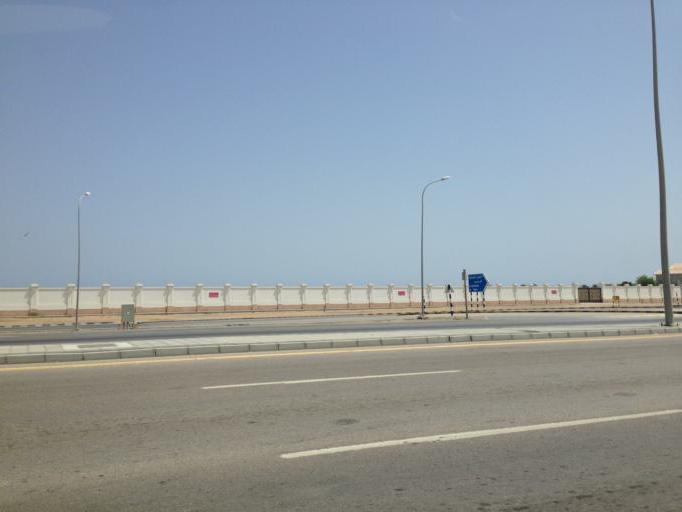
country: OM
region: Muhafazat Masqat
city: Bawshar
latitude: 23.6024
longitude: 58.3462
